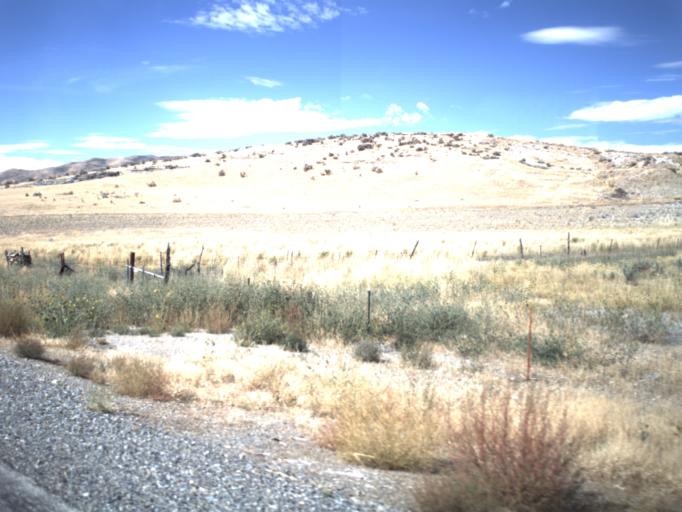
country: US
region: Utah
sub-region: Box Elder County
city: Tremonton
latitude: 41.7224
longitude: -112.4429
